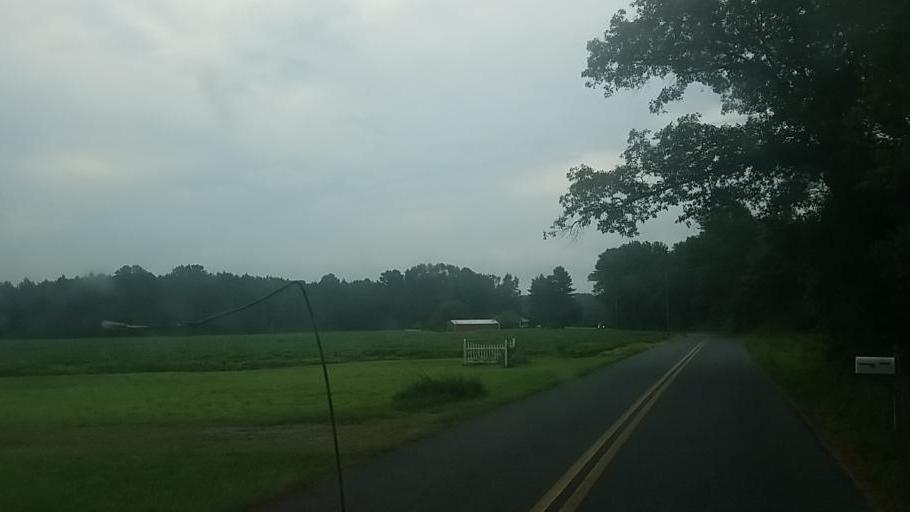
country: US
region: Delaware
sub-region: Sussex County
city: Selbyville
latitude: 38.4256
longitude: -75.2909
